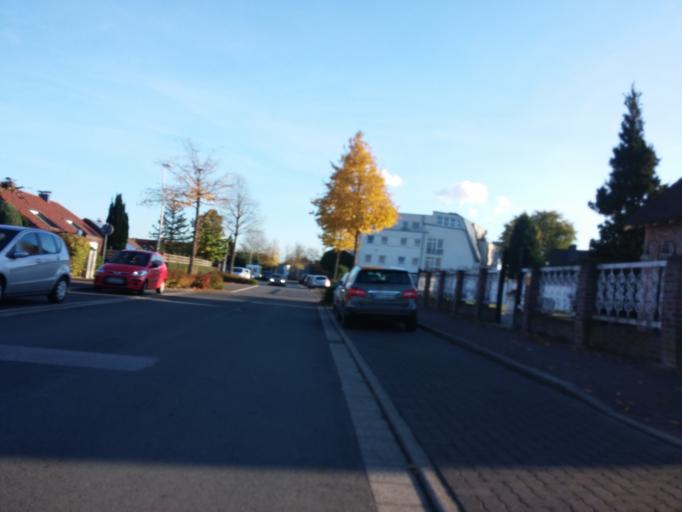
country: DE
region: North Rhine-Westphalia
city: Dorsten
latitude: 51.6538
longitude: 6.9809
